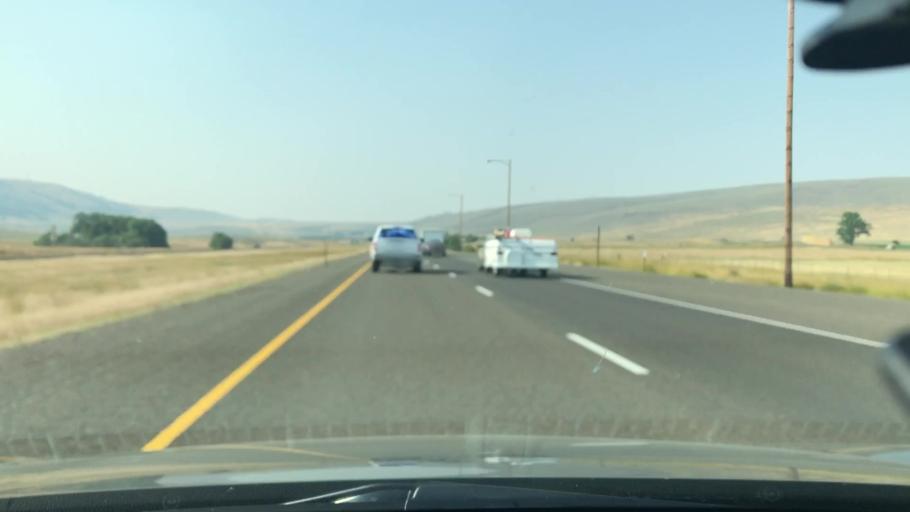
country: US
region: Oregon
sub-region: Union County
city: Union
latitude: 45.1156
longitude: -117.9596
